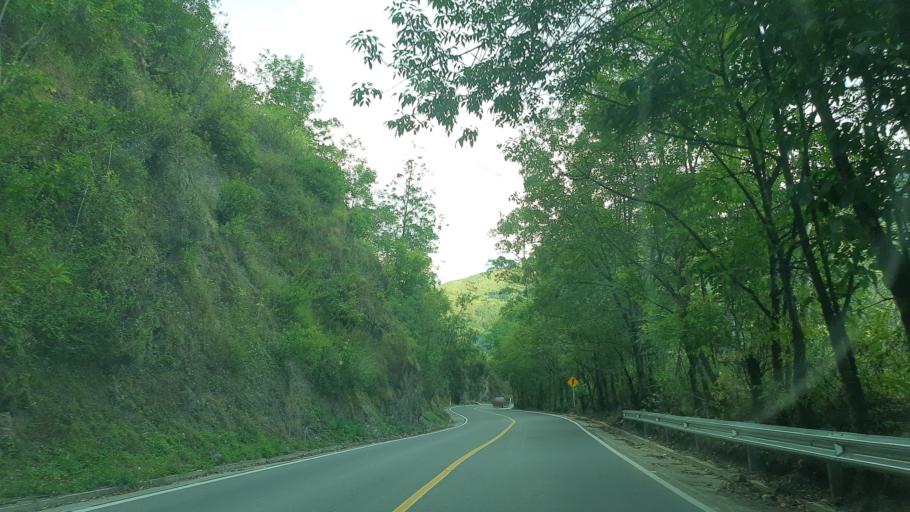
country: CO
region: Boyaca
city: Somondoco
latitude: 5.0101
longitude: -73.4352
